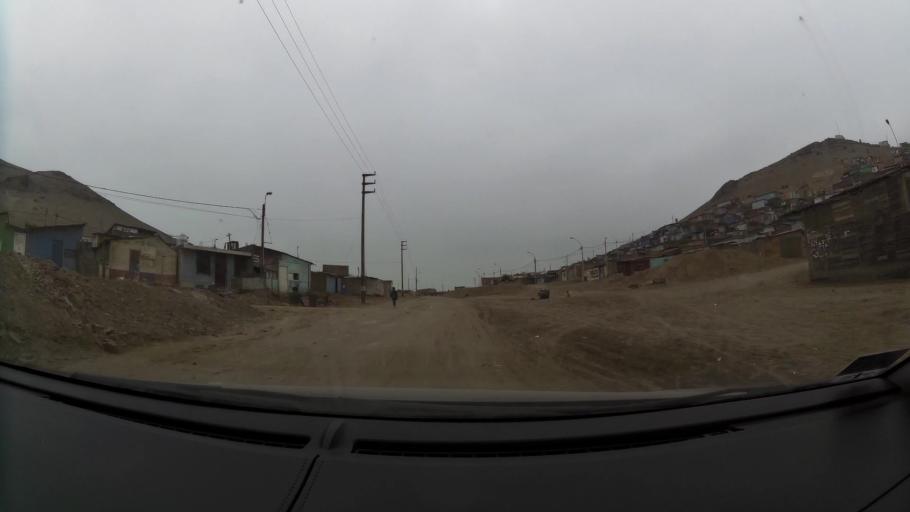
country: PE
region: Lima
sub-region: Lima
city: Santa Rosa
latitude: -11.8280
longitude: -77.1673
